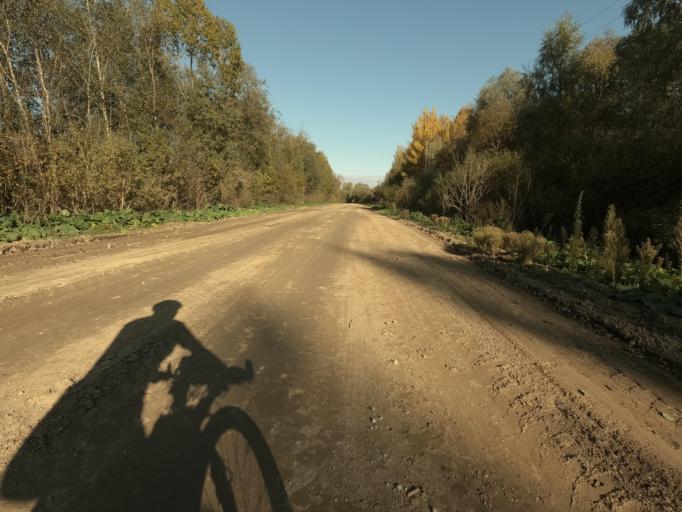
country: RU
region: Novgorod
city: Batetskiy
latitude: 58.8780
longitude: 30.7266
